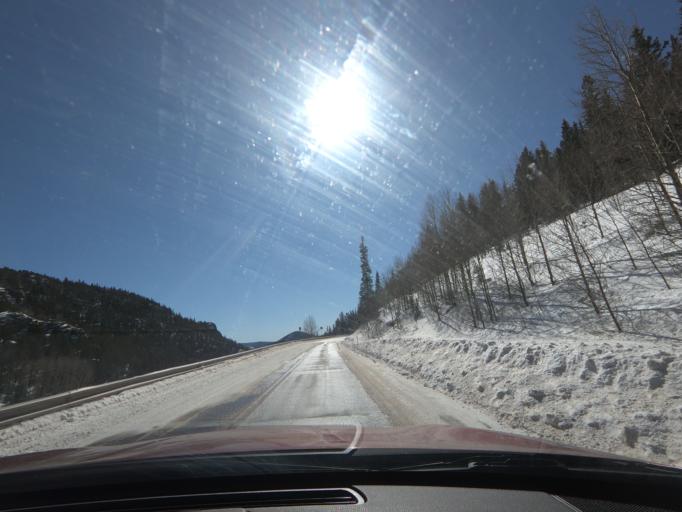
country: US
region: Colorado
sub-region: Teller County
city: Cripple Creek
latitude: 38.7515
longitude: -105.1024
